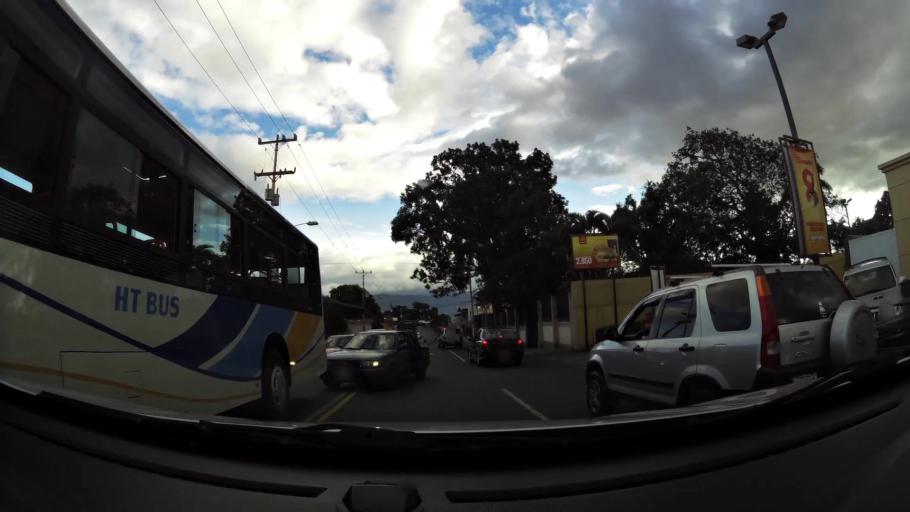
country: CR
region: Alajuela
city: Alajuela
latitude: 10.0123
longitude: -84.2100
